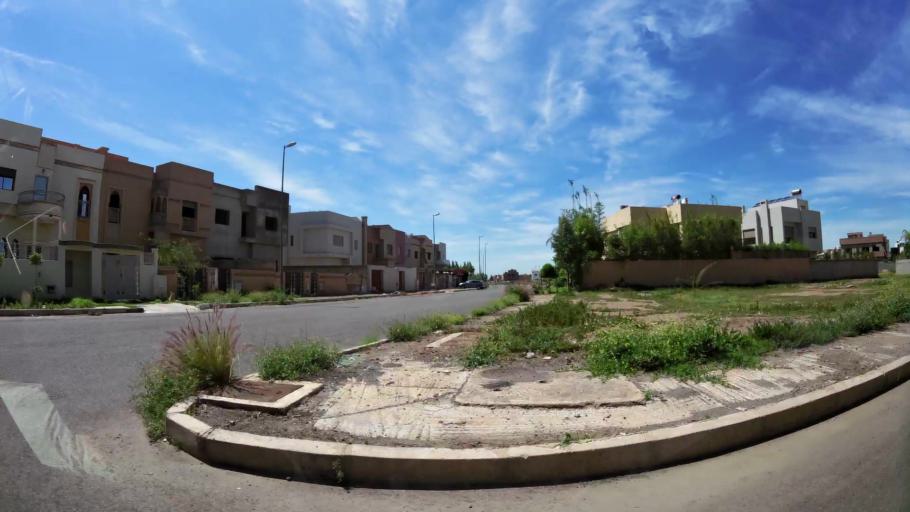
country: MA
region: Marrakech-Tensift-Al Haouz
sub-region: Marrakech
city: Marrakesh
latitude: 31.6518
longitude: -8.0728
